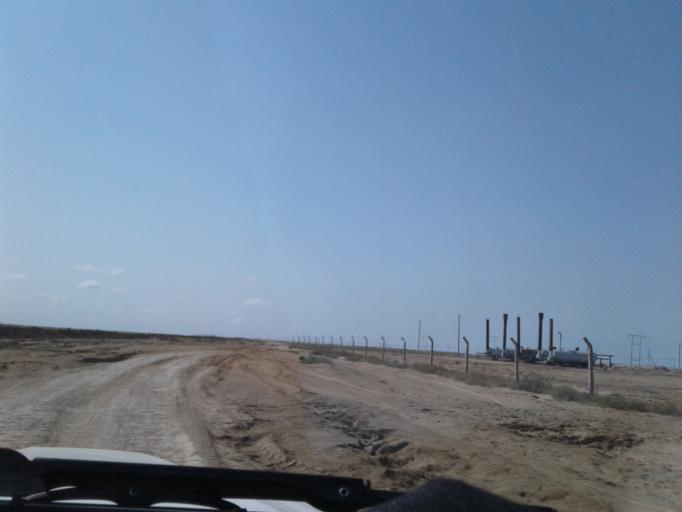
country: IR
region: Golestan
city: Gomishan
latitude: 37.8208
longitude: 53.9224
